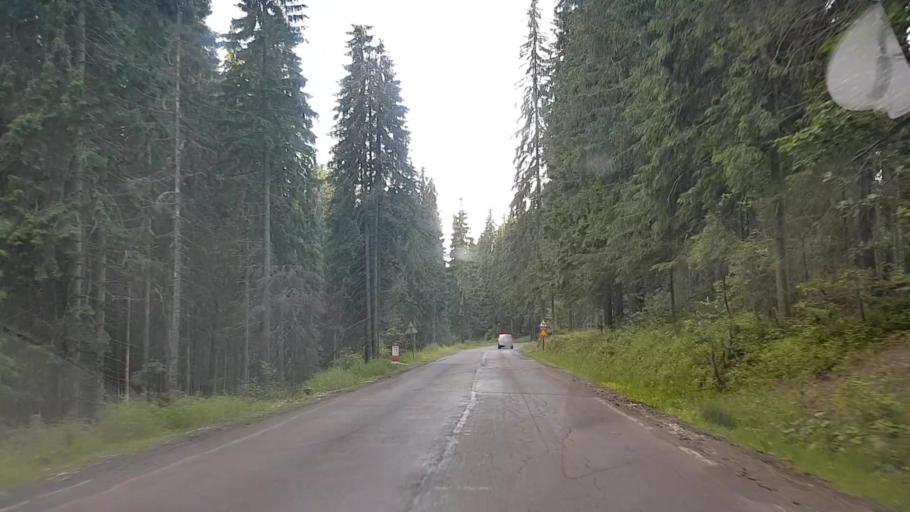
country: RO
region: Harghita
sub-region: Comuna Varsag
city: Varsag
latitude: 46.6531
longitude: 25.2916
